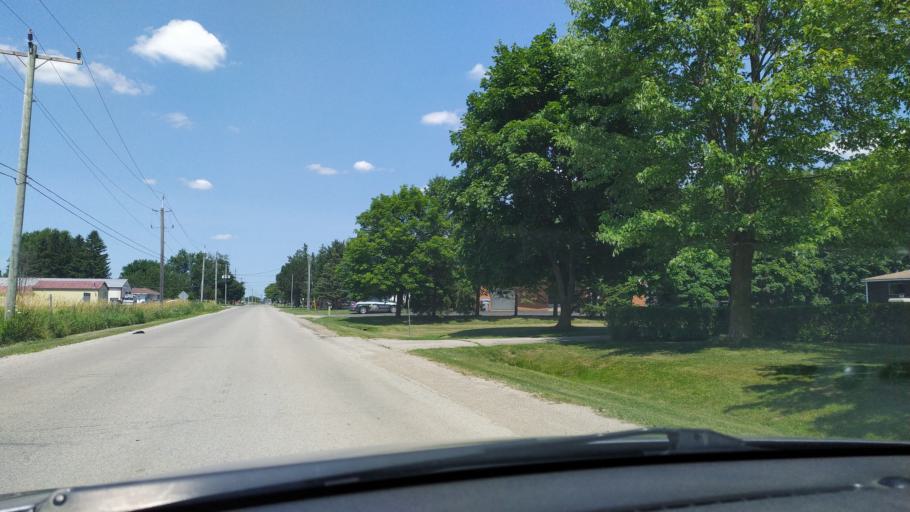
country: CA
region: Ontario
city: Stratford
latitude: 43.3675
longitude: -80.9379
